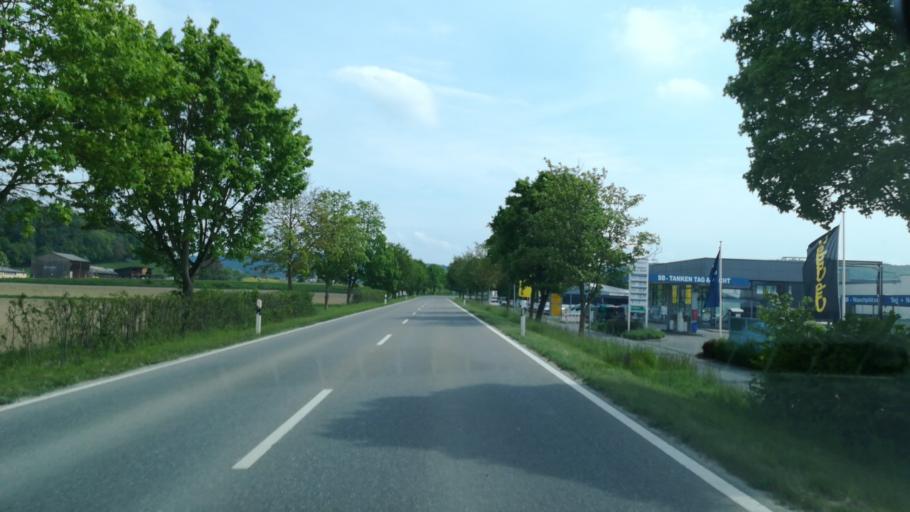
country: DE
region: Baden-Wuerttemberg
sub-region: Freiburg Region
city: Steisslingen
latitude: 47.7820
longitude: 8.9116
